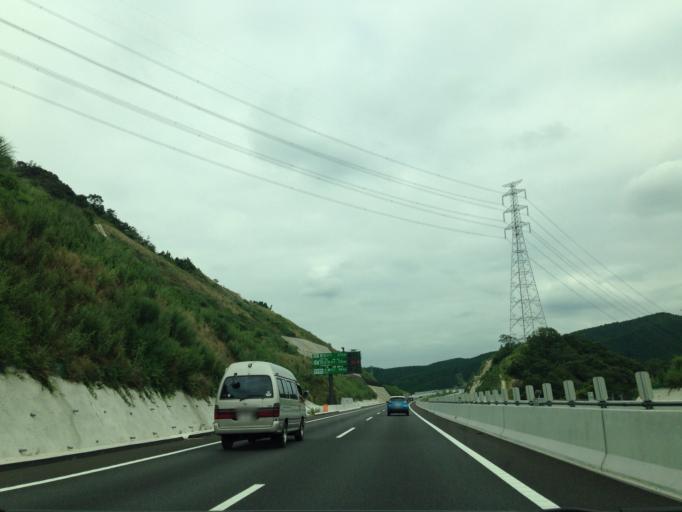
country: JP
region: Aichi
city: Gamagori
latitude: 34.9293
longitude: 137.2664
